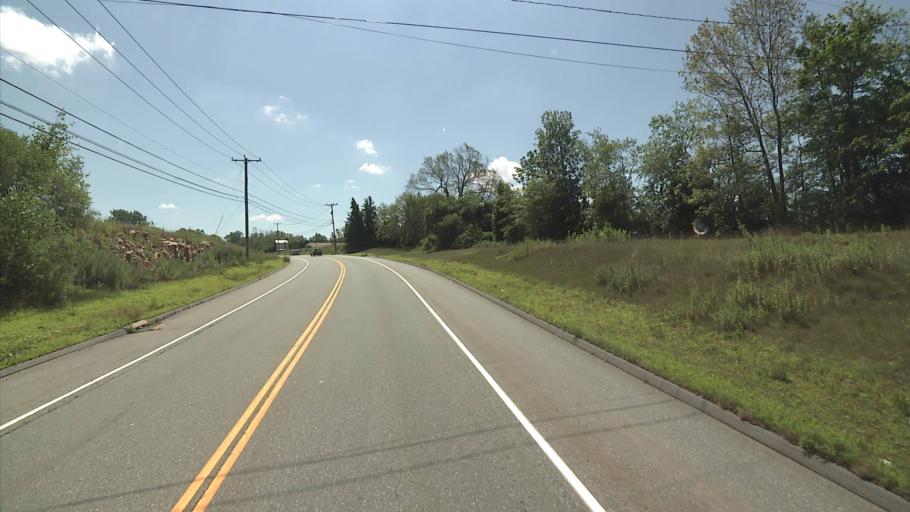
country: US
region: Connecticut
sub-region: Windham County
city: Plainfield
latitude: 41.6793
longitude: -71.8873
